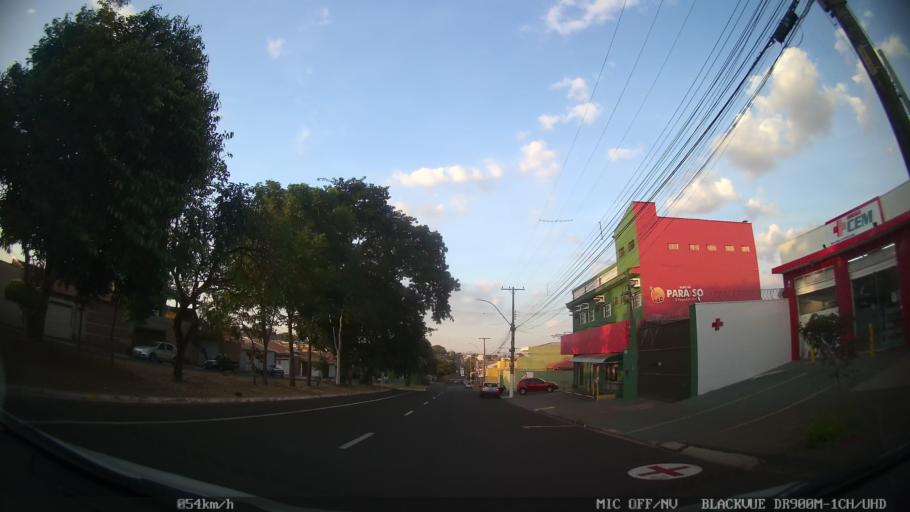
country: BR
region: Sao Paulo
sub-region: Ribeirao Preto
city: Ribeirao Preto
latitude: -21.1403
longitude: -47.8538
